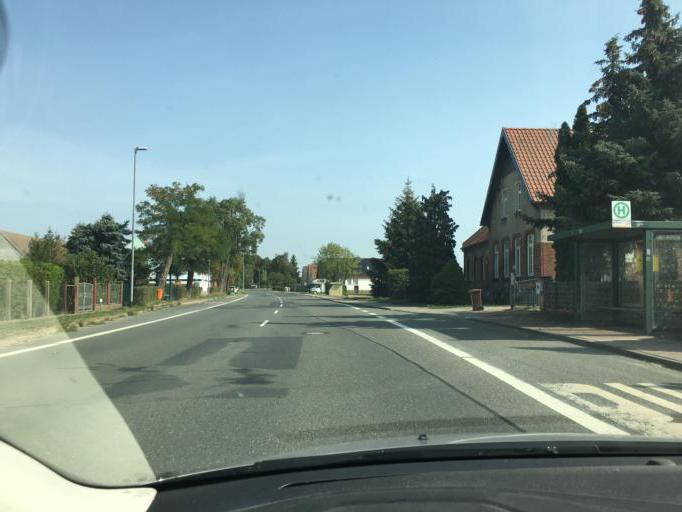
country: DE
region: Saxony-Anhalt
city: Barby
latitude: 51.9931
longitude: 11.8346
